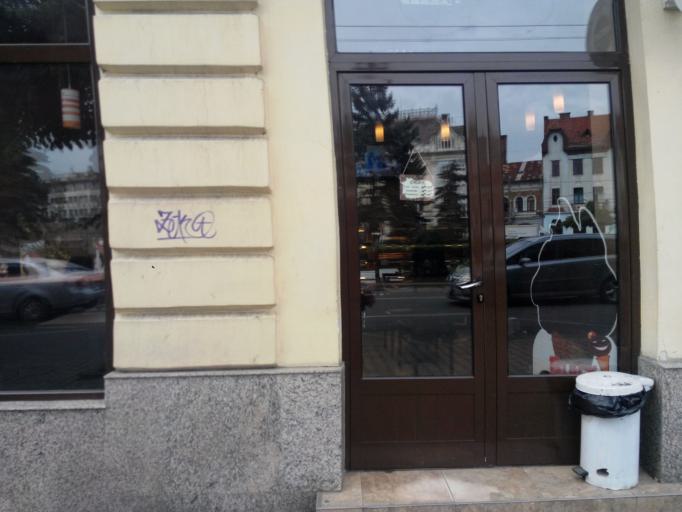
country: RO
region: Cluj
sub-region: Municipiul Cluj-Napoca
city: Cluj-Napoca
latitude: 46.7741
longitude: 23.5895
